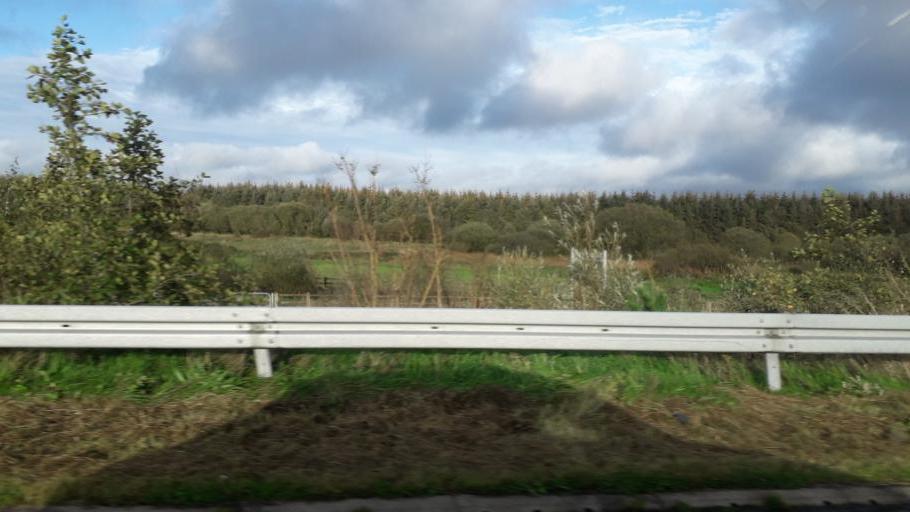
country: IE
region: Connaught
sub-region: Roscommon
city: Ballaghaderreen
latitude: 53.9082
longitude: -8.5474
